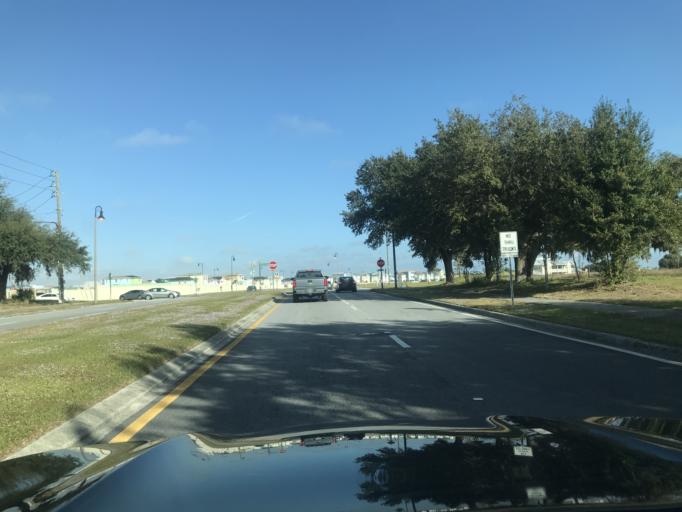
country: US
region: Florida
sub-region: Polk County
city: Citrus Ridge
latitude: 28.3319
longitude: -81.6071
